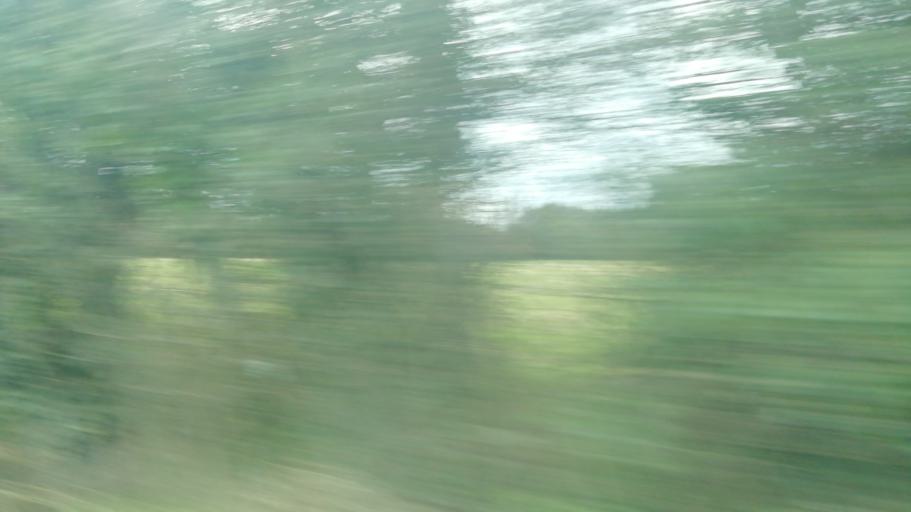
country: IE
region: Leinster
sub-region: Kildare
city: Prosperous
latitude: 53.3078
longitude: -6.7229
